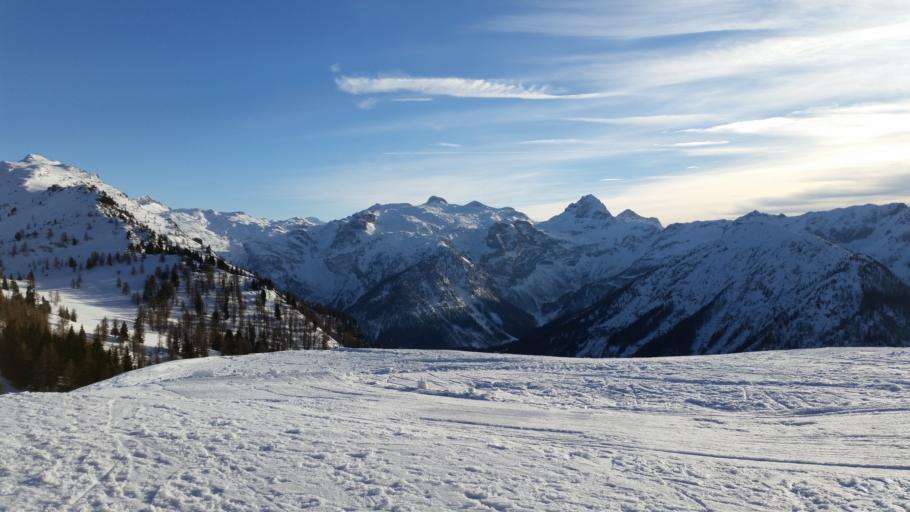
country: AT
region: Salzburg
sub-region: Politischer Bezirk Sankt Johann im Pongau
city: Flachau
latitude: 47.2936
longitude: 13.4287
